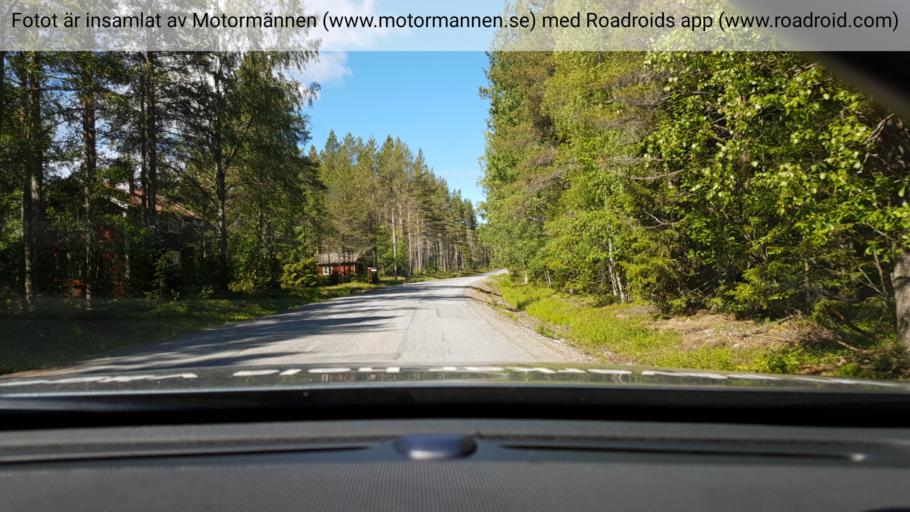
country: SE
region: Vaesterbotten
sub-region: Skelleftea Kommun
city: Burea
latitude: 64.4477
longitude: 21.4676
